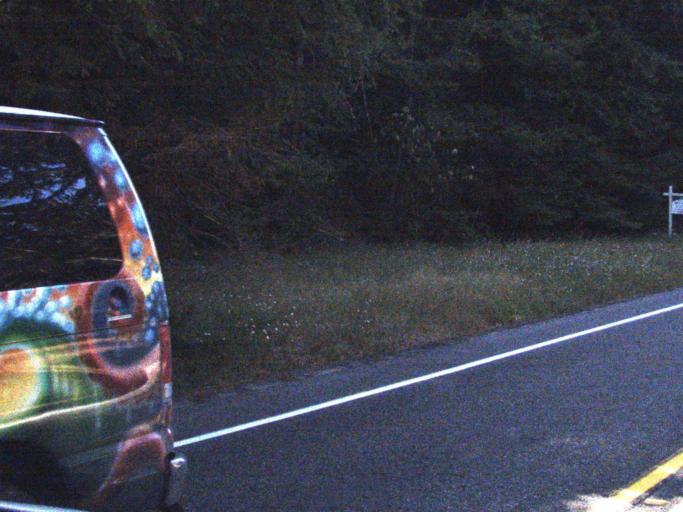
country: US
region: Washington
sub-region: King County
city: Riverbend
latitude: 47.1063
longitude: -121.5953
